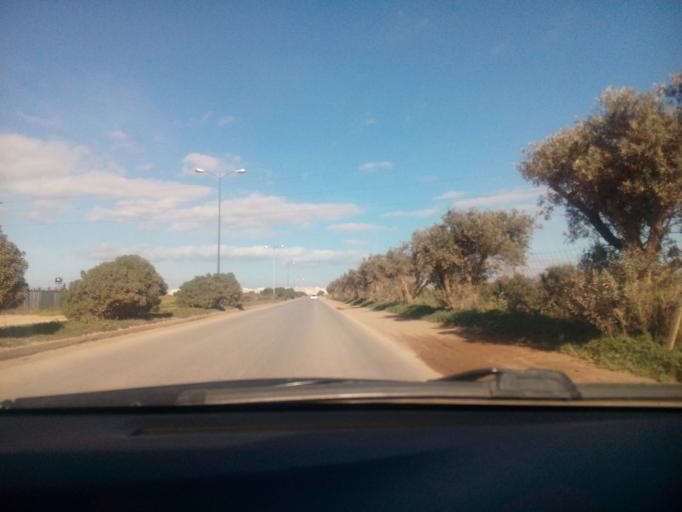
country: DZ
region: Oran
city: Sidi ech Chahmi
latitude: 35.6578
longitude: -0.5675
